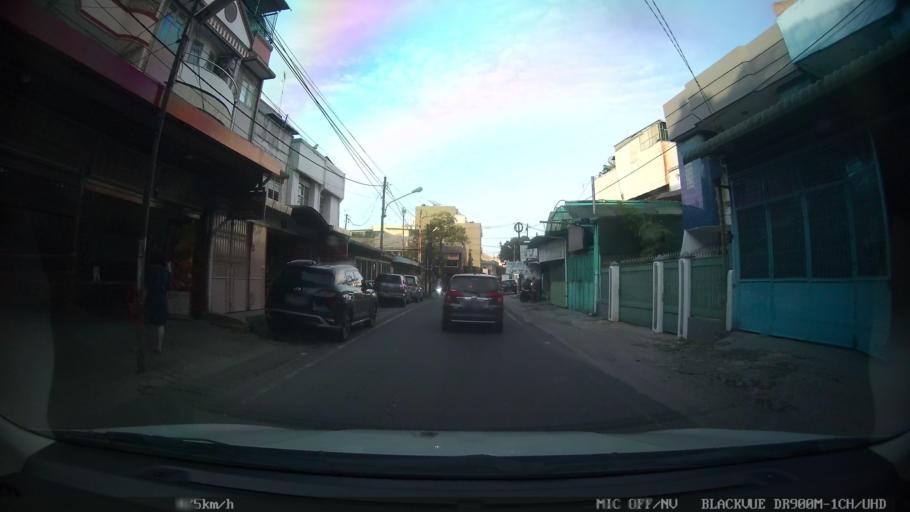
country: ID
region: North Sumatra
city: Medan
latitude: 3.5890
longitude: 98.6670
